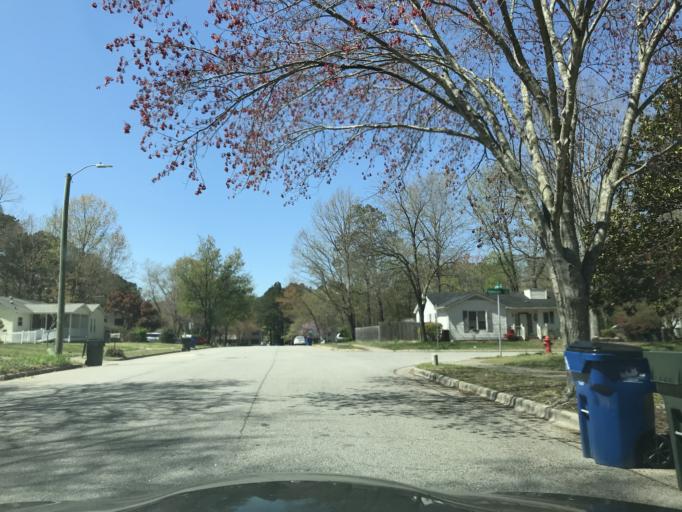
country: US
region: North Carolina
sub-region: Wake County
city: Raleigh
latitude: 35.8330
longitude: -78.5776
